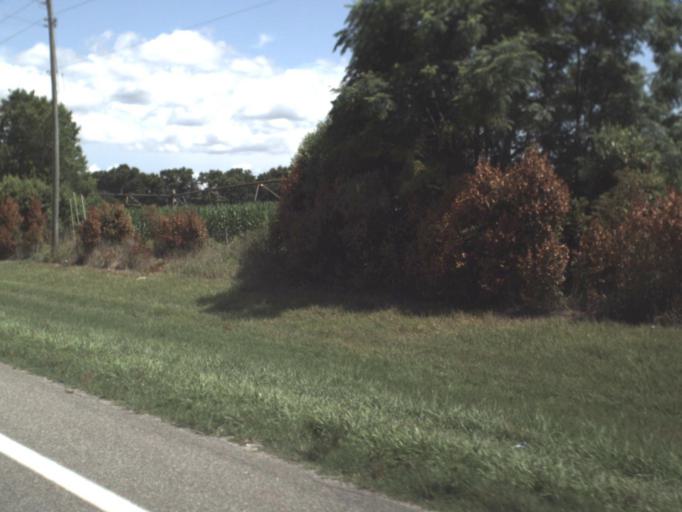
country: US
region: Florida
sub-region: Lafayette County
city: Mayo
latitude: 30.0018
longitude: -83.0223
